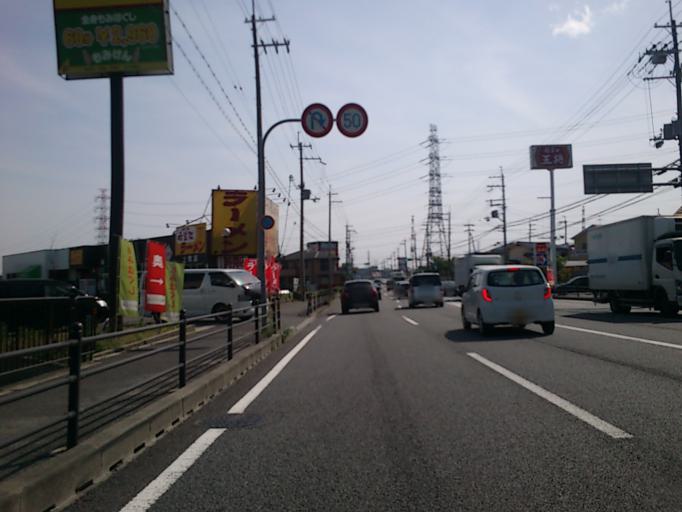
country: JP
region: Kyoto
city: Yawata
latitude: 34.8697
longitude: 135.6615
